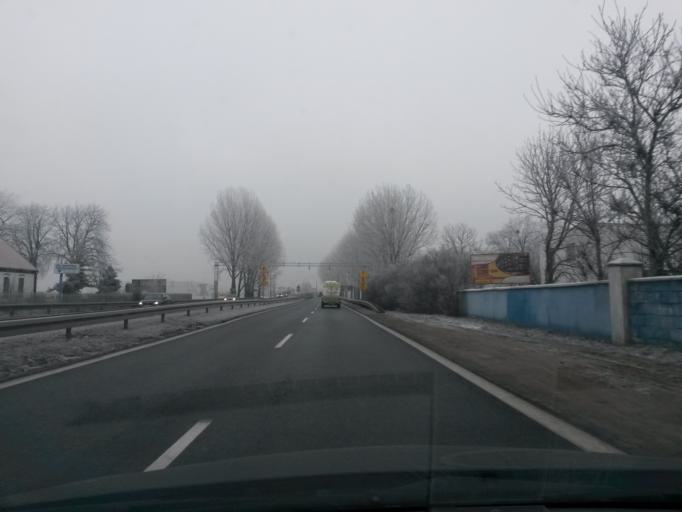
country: PL
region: Greater Poland Voivodeship
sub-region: Powiat poznanski
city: Kostrzyn
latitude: 52.3973
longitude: 17.1996
